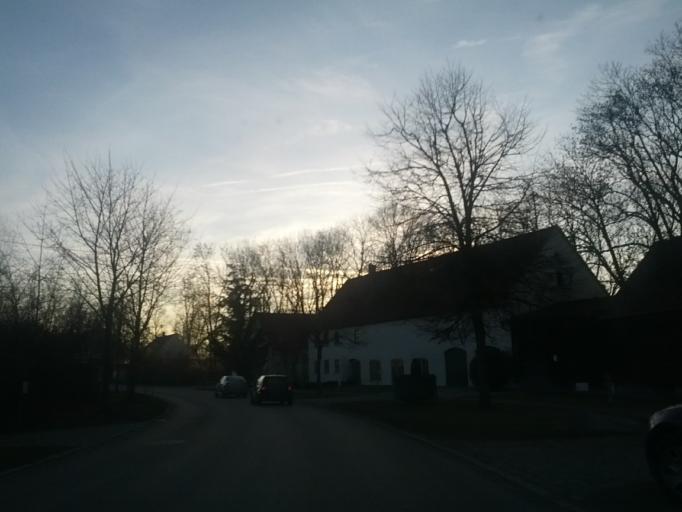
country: DE
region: Bavaria
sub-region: Swabia
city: Fellheim
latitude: 48.0887
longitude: 10.1510
